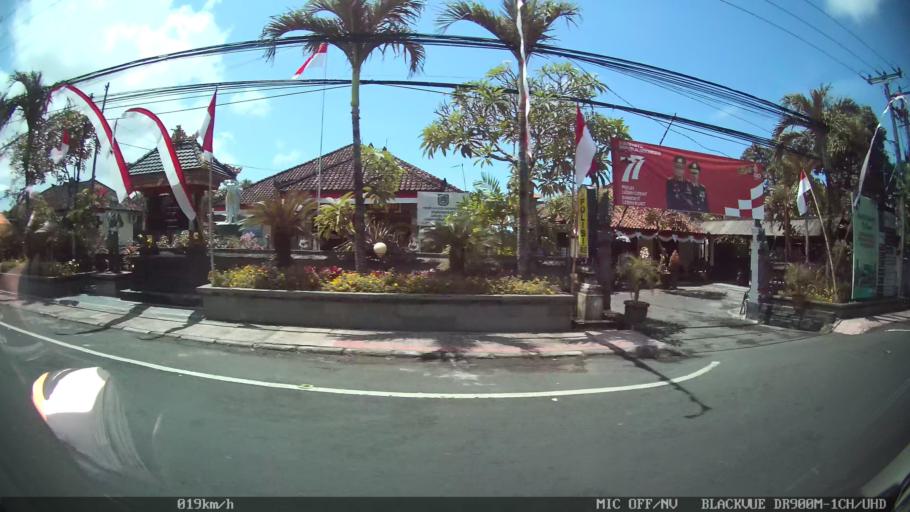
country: ID
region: Bali
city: Banjar Pasekan
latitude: -8.5951
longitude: 115.2828
